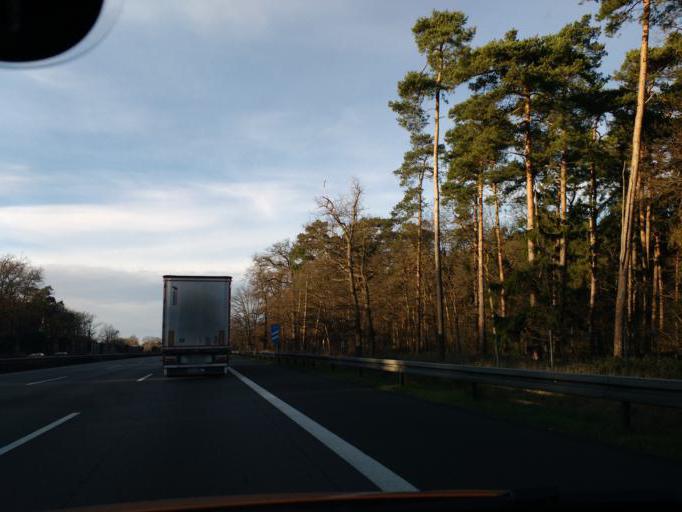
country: DE
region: Lower Saxony
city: Lehrte
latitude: 52.3860
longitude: 10.0061
